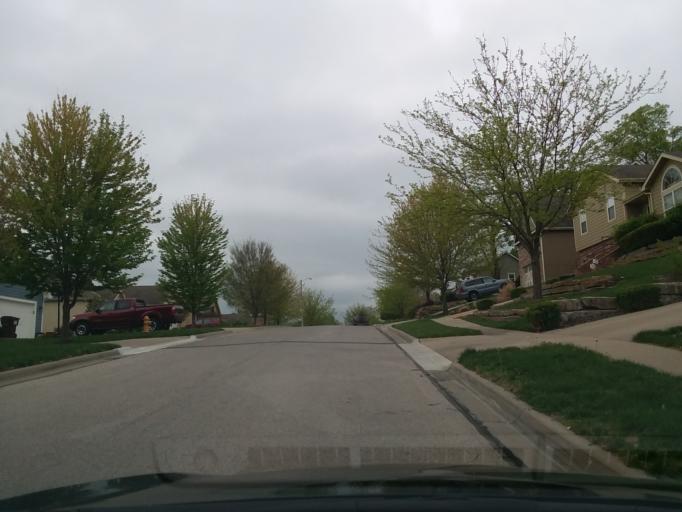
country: US
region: Kansas
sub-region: Douglas County
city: Lawrence
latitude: 38.9959
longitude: -95.2876
